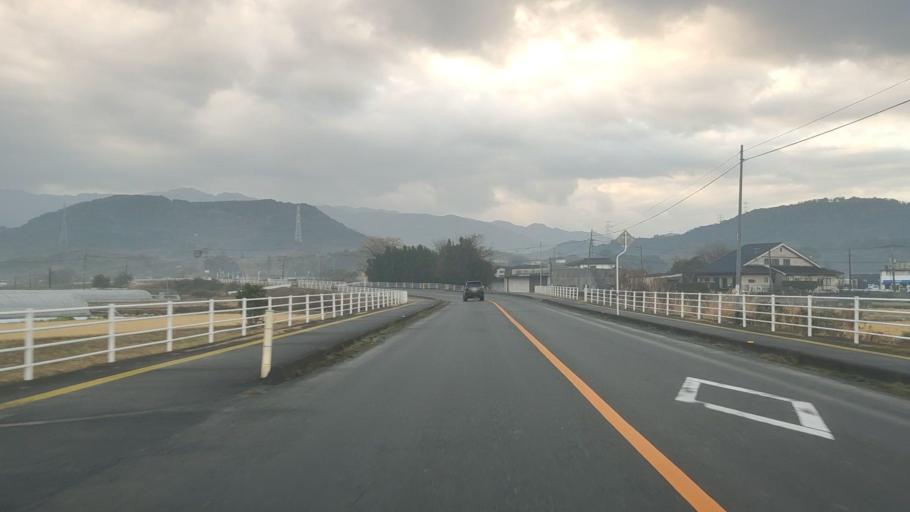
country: JP
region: Kumamoto
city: Matsubase
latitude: 32.6459
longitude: 130.8117
